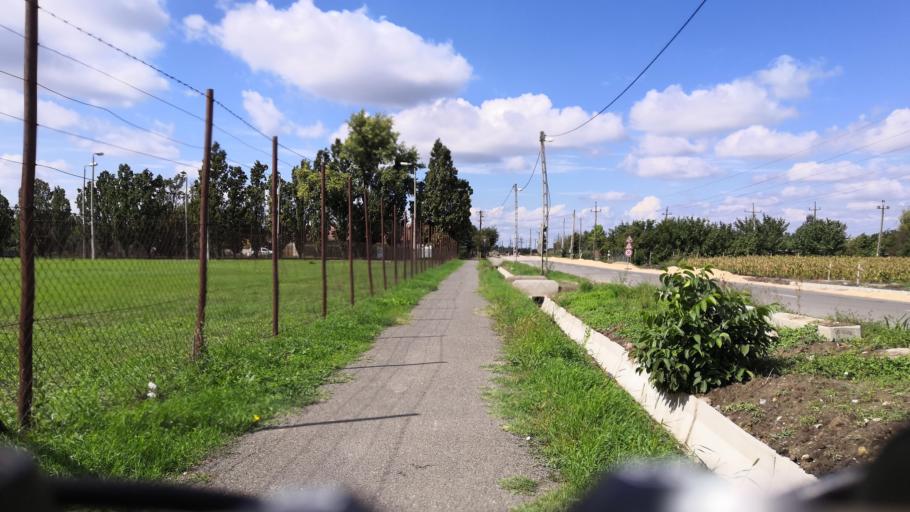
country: HU
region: Csongrad
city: Szeged
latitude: 46.2790
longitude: 20.1299
